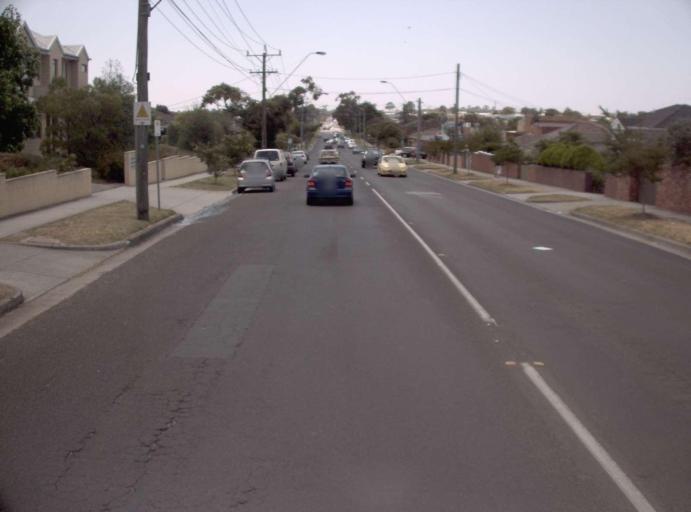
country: AU
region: Victoria
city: Highett
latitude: -37.9575
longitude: 145.0571
